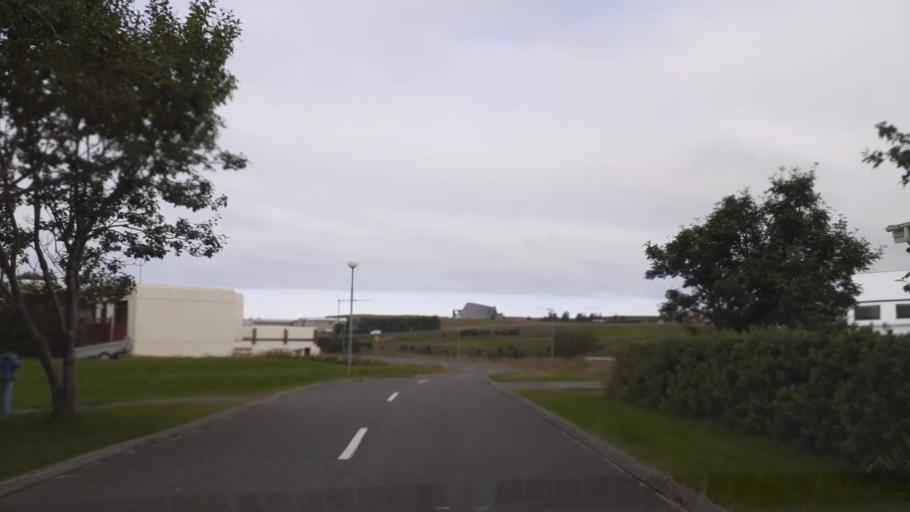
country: IS
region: Northwest
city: Saudarkrokur
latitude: 65.6562
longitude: -20.2781
